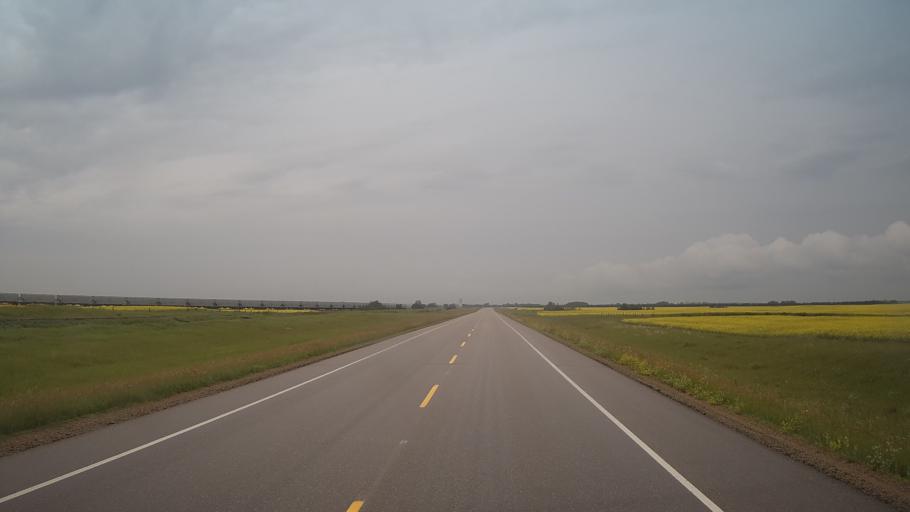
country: CA
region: Saskatchewan
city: Wilkie
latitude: 52.3023
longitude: -108.6765
